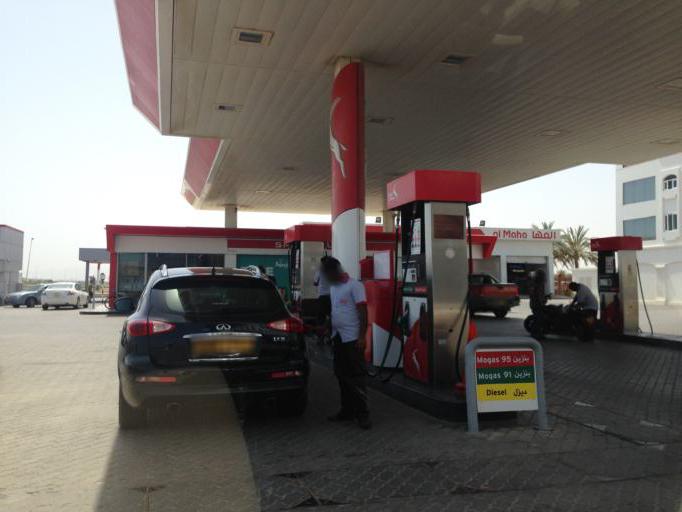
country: OM
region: Muhafazat Masqat
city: As Sib al Jadidah
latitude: 23.6249
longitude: 58.2616
